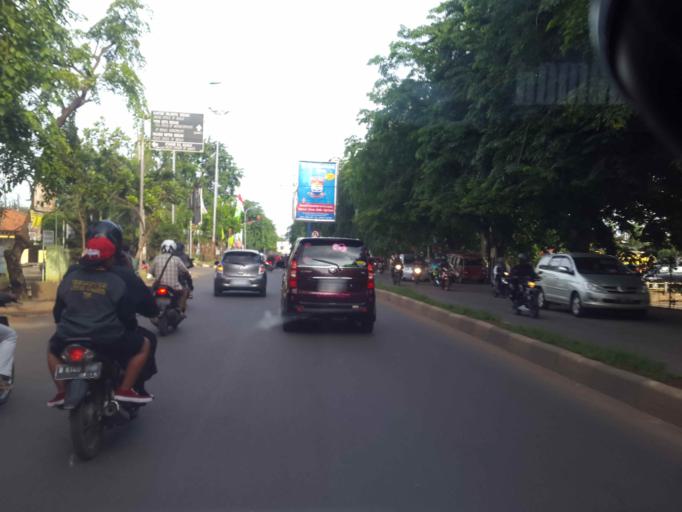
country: ID
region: West Java
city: Bekasi
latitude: -6.2493
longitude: 106.9621
